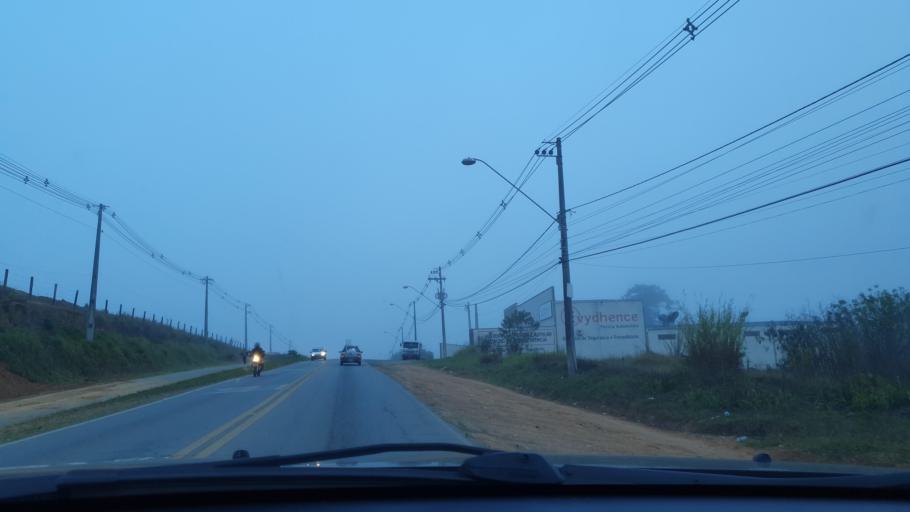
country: BR
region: Sao Paulo
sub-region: Ibiuna
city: Ibiuna
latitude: -23.6671
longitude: -47.2278
